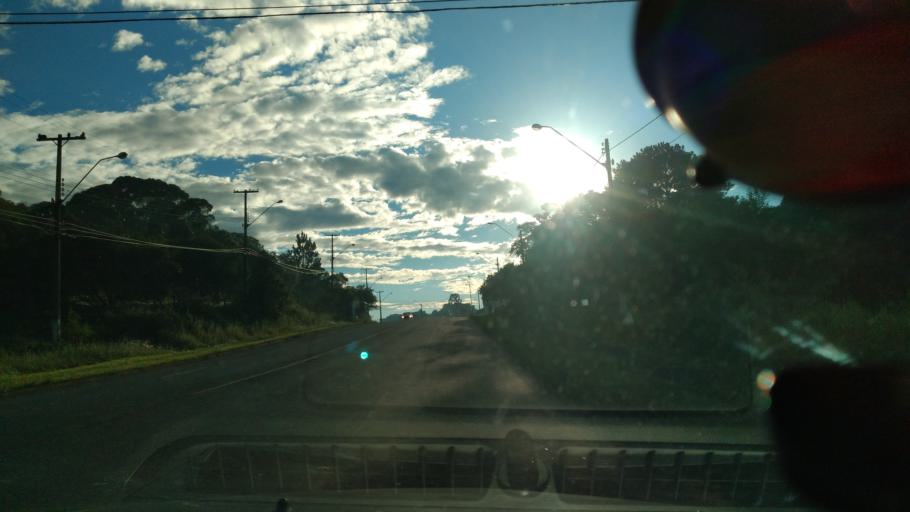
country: BR
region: Parana
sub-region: Guarapuava
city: Guarapuava
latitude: -25.3942
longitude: -51.4844
